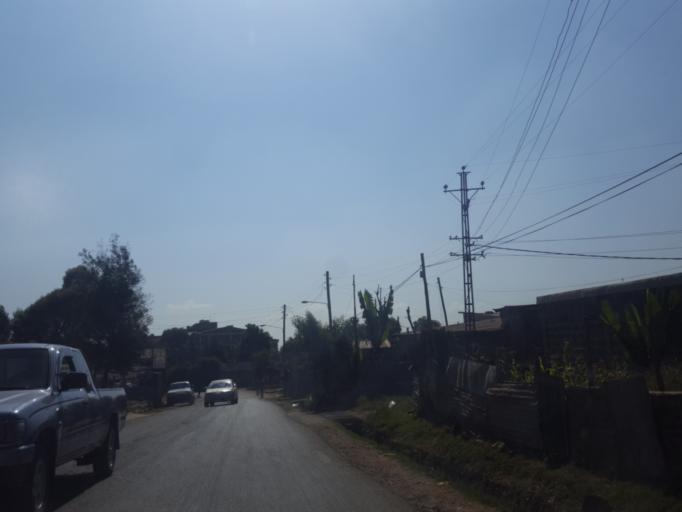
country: ET
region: Adis Abeba
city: Addis Ababa
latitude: 9.0496
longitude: 38.7354
